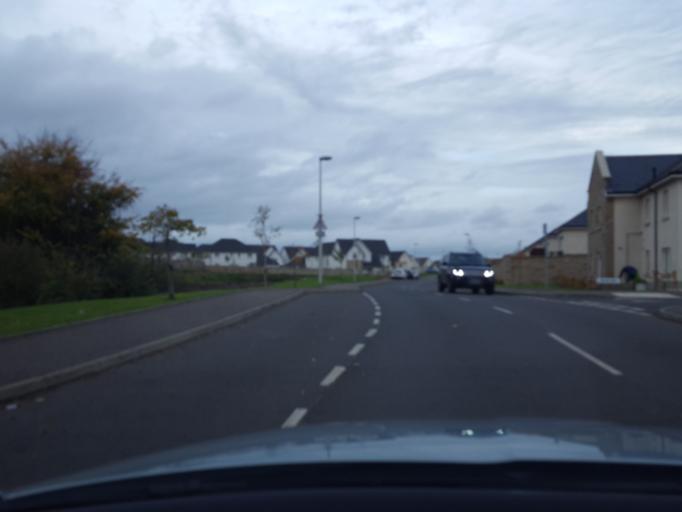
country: GB
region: Scotland
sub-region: Edinburgh
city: Ratho
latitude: 55.9244
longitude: -3.3794
